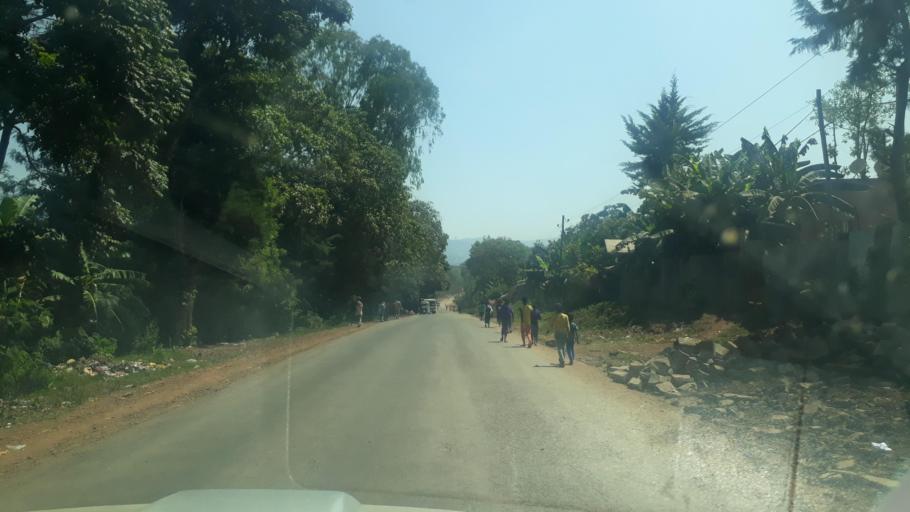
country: ET
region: Oromiya
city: Jima
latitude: 7.7006
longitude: 36.8103
